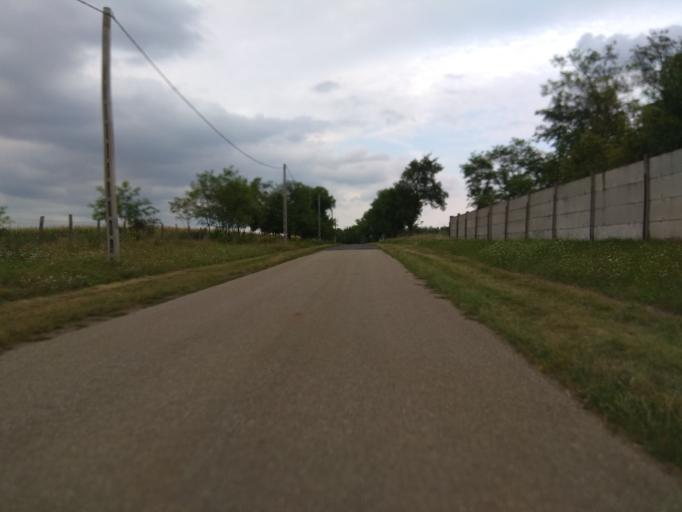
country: HU
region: Borsod-Abauj-Zemplen
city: Gesztely
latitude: 48.1379
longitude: 21.0094
